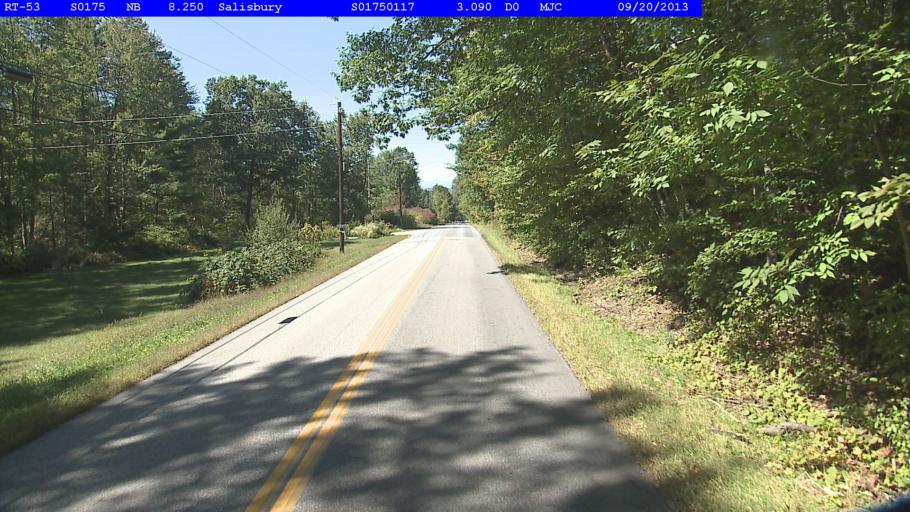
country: US
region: Vermont
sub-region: Addison County
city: Middlebury (village)
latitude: 43.9225
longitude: -73.0916
